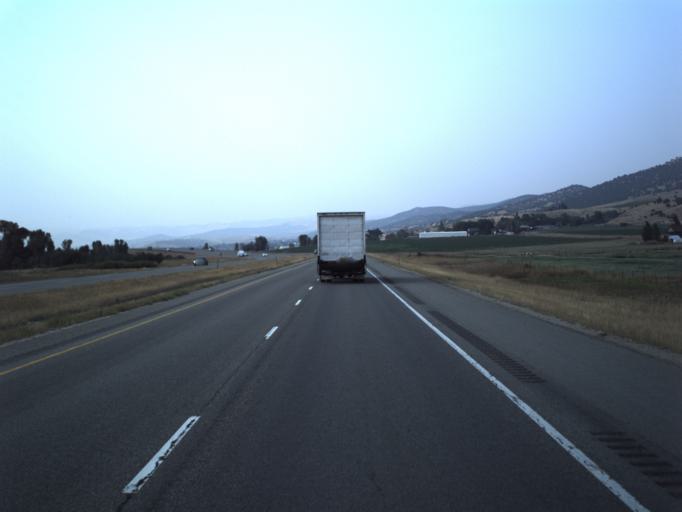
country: US
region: Utah
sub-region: Summit County
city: Coalville
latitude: 40.8385
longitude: -111.3882
